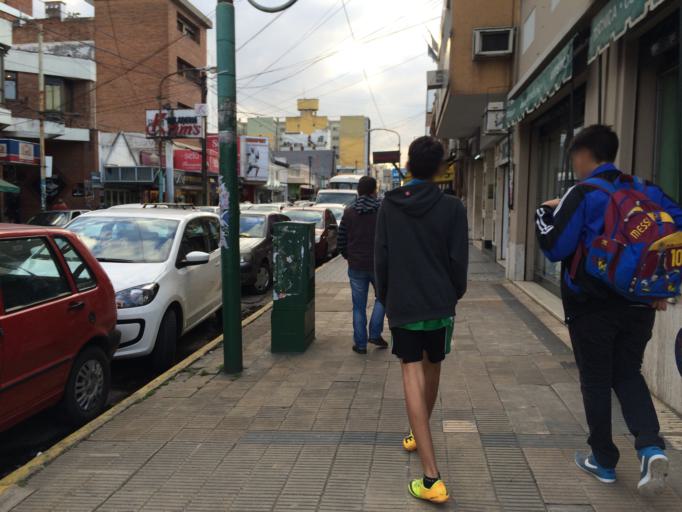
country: AR
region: Buenos Aires
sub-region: Partido de Lomas de Zamora
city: Lomas de Zamora
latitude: -34.7436
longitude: -58.3902
